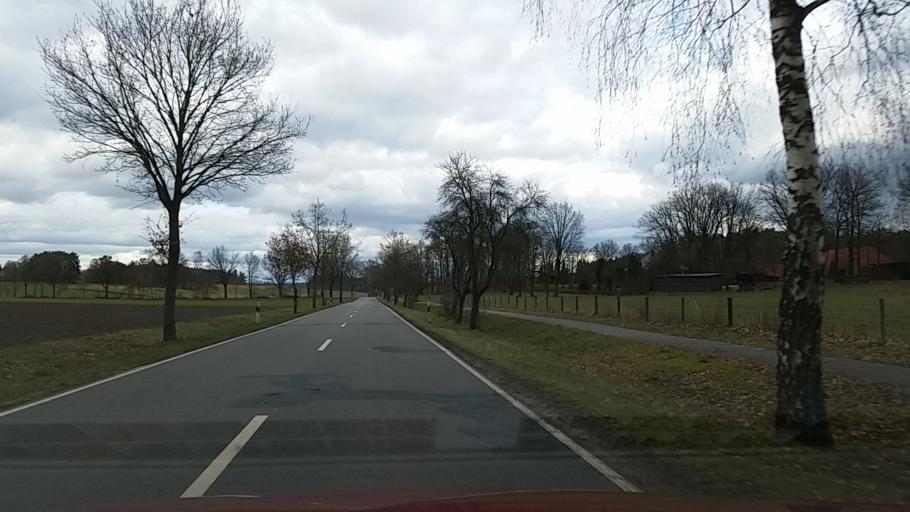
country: DE
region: Lower Saxony
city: Karwitz
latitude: 53.1117
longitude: 10.9477
